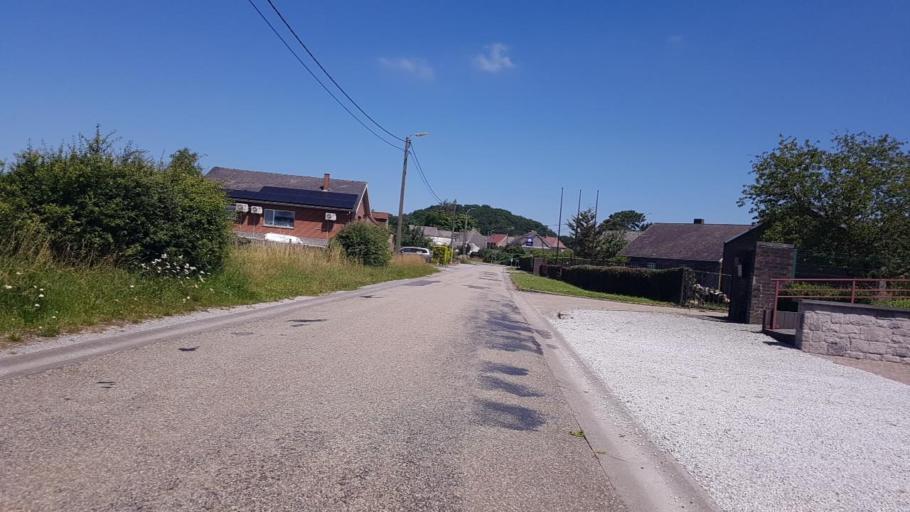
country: BE
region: Wallonia
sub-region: Province du Hainaut
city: Froidchapelle
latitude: 50.1442
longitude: 4.2657
